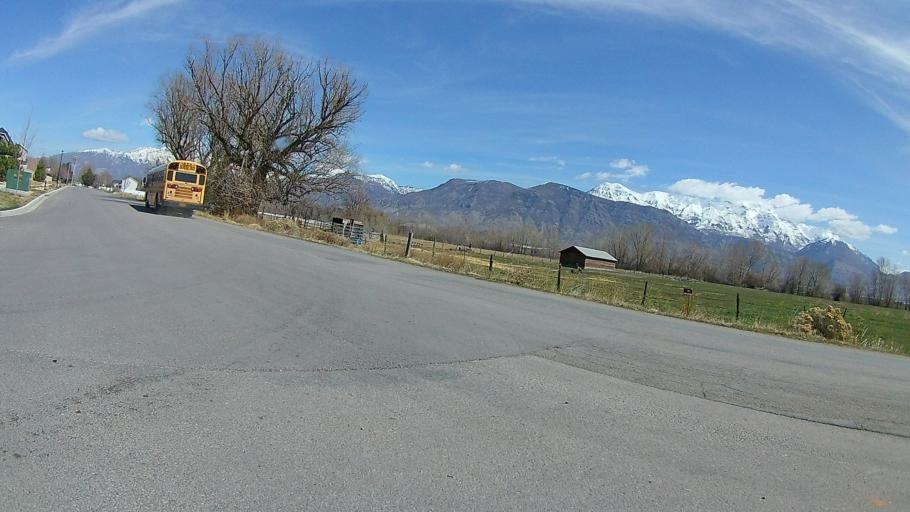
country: US
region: Utah
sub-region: Utah County
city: American Fork
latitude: 40.3626
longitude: -111.8015
